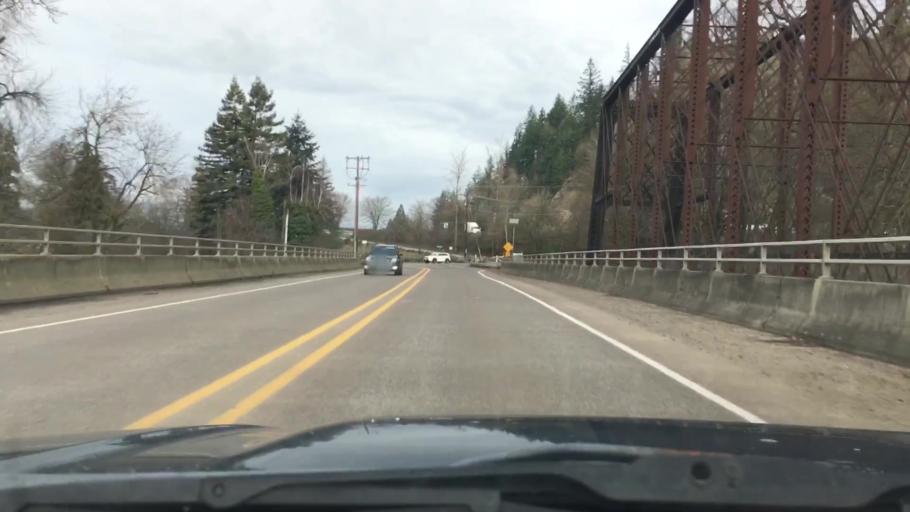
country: US
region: Oregon
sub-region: Lane County
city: Coburg
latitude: 44.1125
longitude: -123.0472
